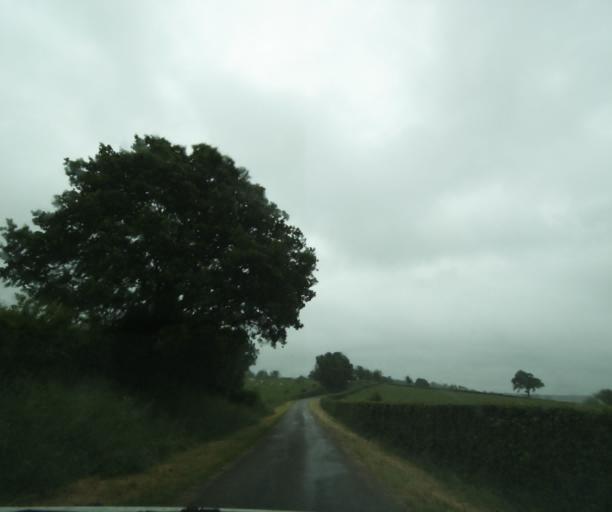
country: FR
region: Bourgogne
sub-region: Departement de Saone-et-Loire
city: Palinges
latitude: 46.5046
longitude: 4.1878
